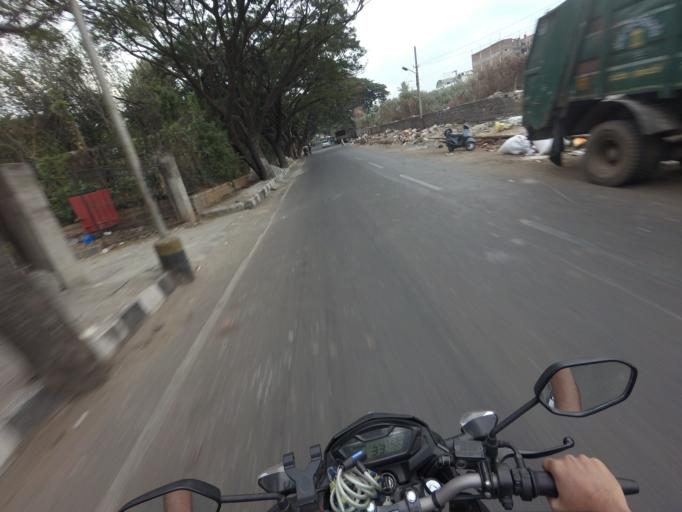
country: IN
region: Karnataka
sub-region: Bangalore Urban
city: Bangalore
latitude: 12.9611
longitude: 77.5413
